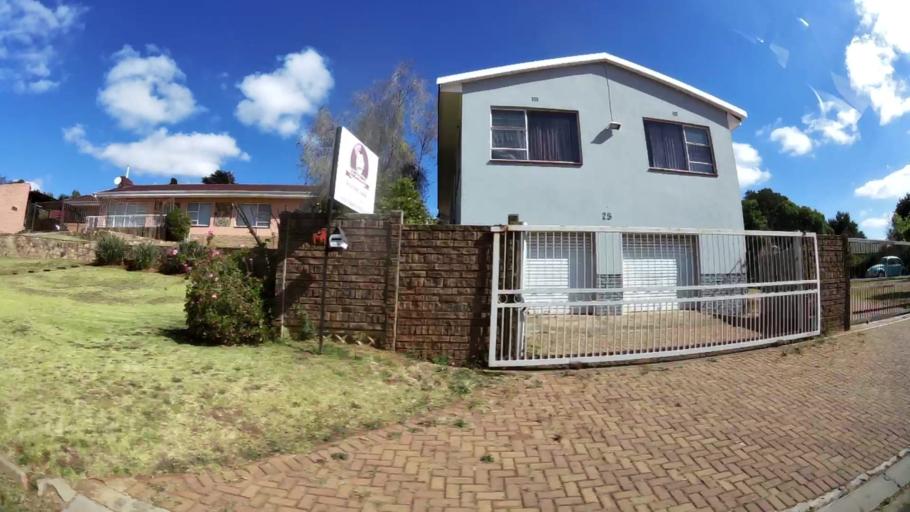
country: ZA
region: Gauteng
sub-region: West Rand District Municipality
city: Krugersdorp
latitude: -26.0943
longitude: 27.7977
